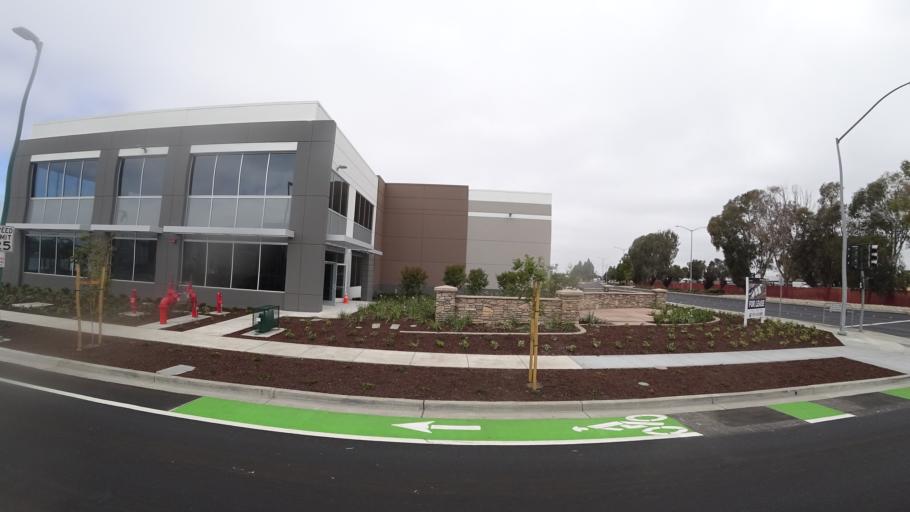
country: US
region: California
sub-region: Alameda County
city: Hayward
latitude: 37.6163
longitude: -122.0924
